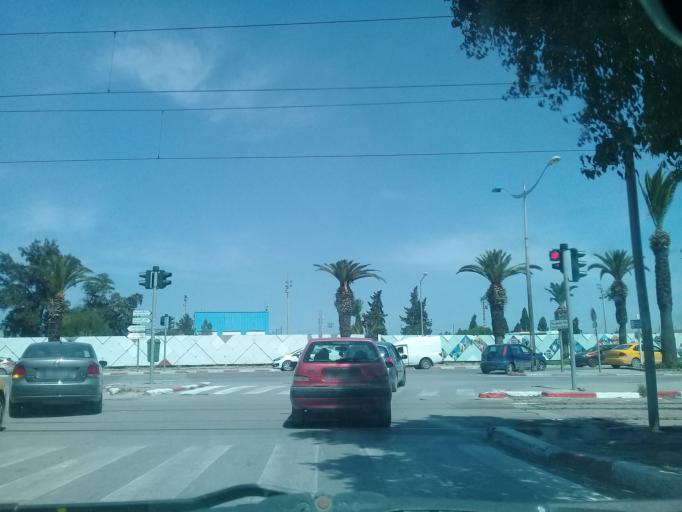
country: TN
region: Tunis
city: Tunis
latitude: 36.8137
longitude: 10.1836
